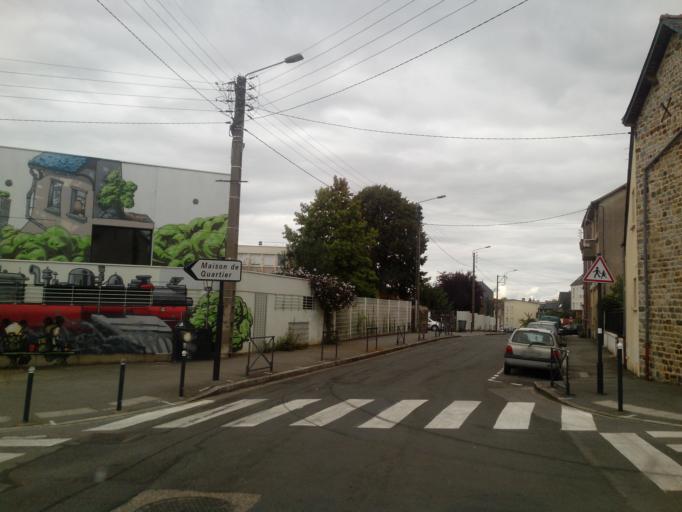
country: FR
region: Brittany
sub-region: Departement d'Ille-et-Vilaine
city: Rennes
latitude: 48.0983
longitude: -1.6689
